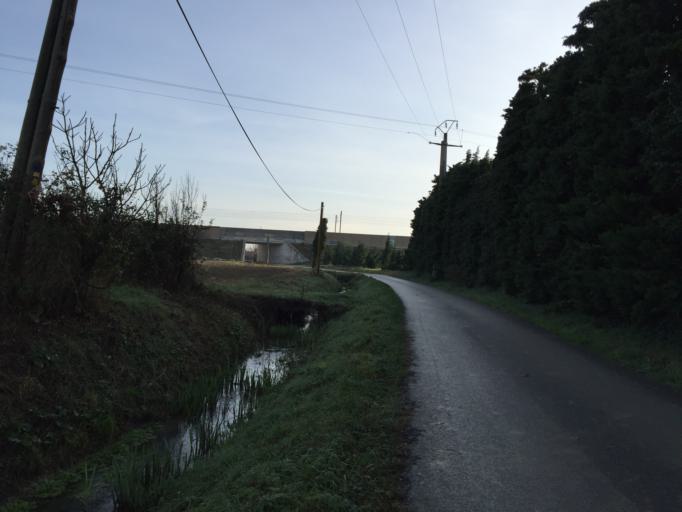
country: FR
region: Provence-Alpes-Cote d'Azur
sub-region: Departement du Vaucluse
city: Caderousse
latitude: 44.1199
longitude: 4.7710
